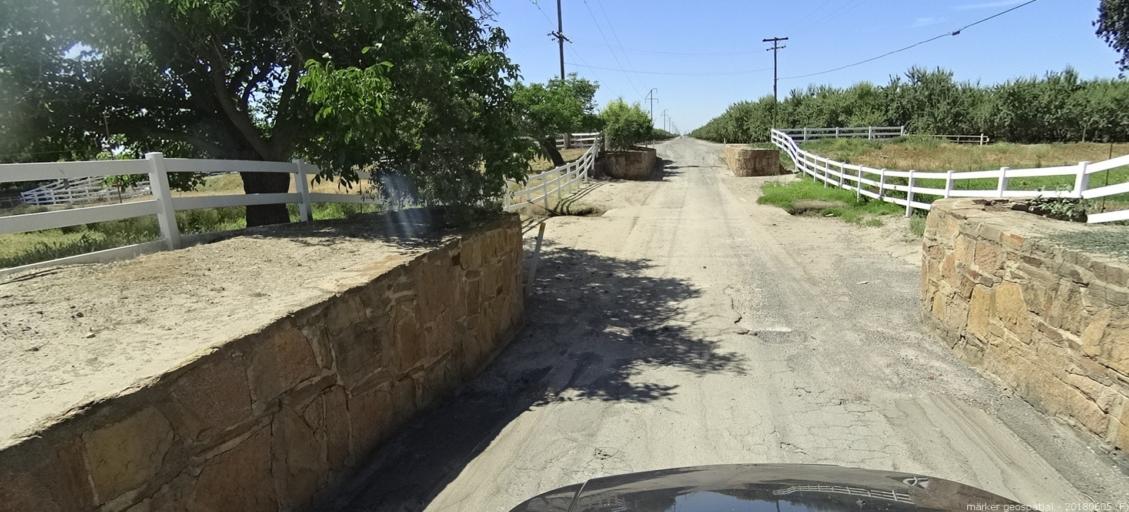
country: US
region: California
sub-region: Madera County
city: Chowchilla
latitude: 37.1239
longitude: -120.3471
